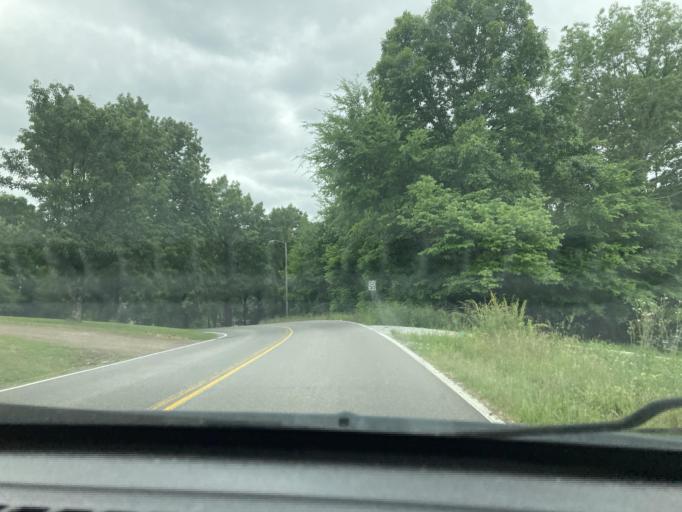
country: US
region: Tennessee
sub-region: Dickson County
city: Dickson
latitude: 36.0966
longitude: -87.3808
